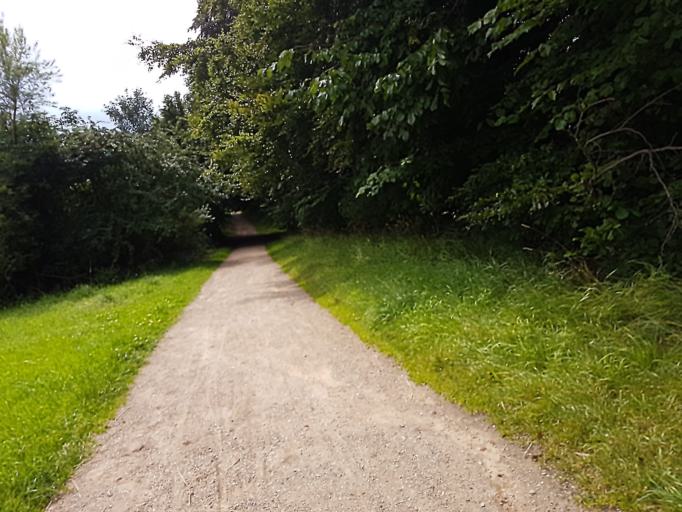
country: DK
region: Capital Region
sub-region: Fureso Kommune
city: Vaerlose
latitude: 55.7918
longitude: 12.3591
